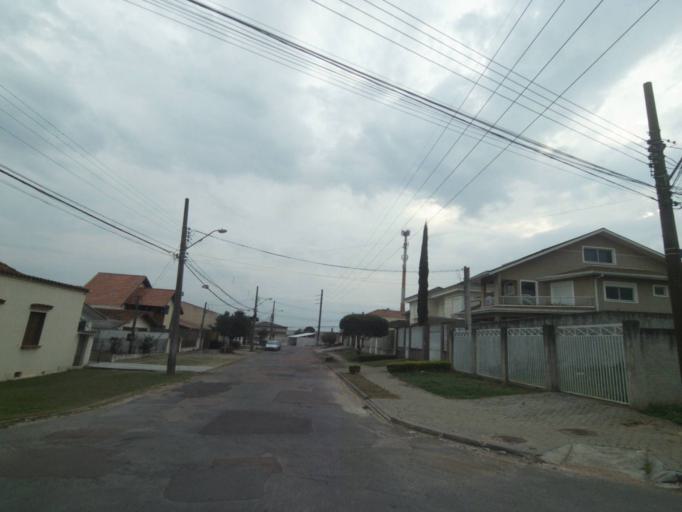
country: BR
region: Parana
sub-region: Pinhais
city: Pinhais
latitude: -25.4709
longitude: -49.2357
